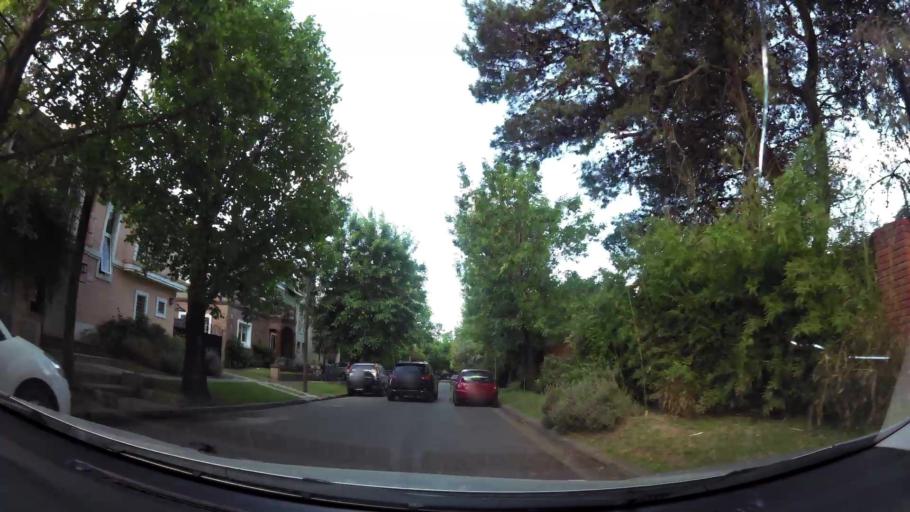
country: AR
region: Buenos Aires
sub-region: Partido de Tigre
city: Tigre
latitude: -34.4701
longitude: -58.5607
